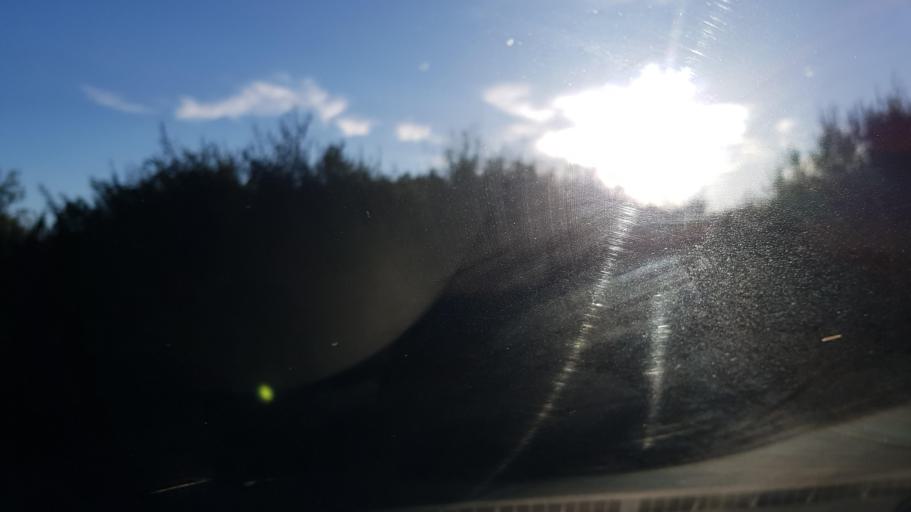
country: IT
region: Apulia
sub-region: Provincia di Lecce
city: Giorgilorio
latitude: 40.4586
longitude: 18.2134
